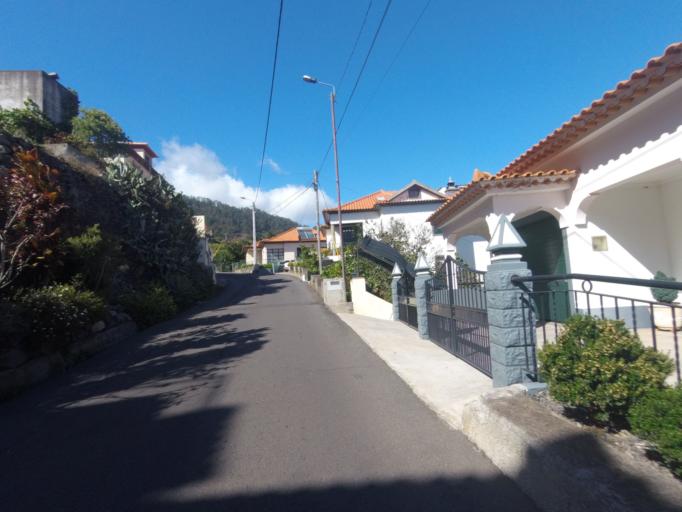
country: PT
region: Madeira
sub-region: Ribeira Brava
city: Campanario
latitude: 32.6730
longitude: -17.0317
